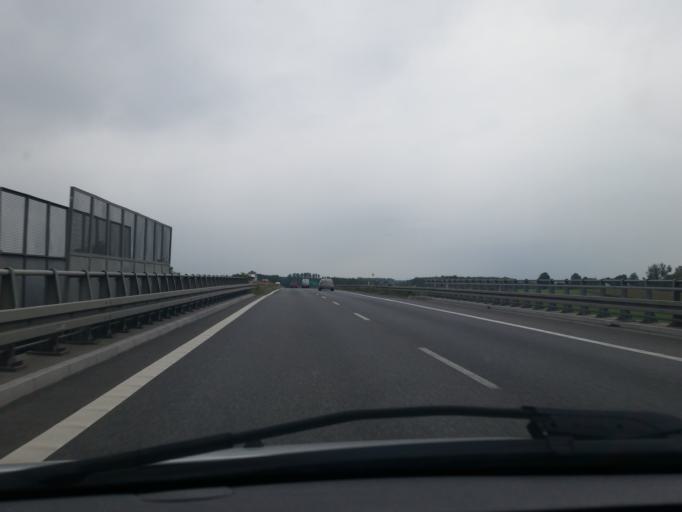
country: PL
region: Masovian Voivodeship
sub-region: Powiat zyrardowski
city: Mszczonow
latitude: 51.9675
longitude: 20.5014
